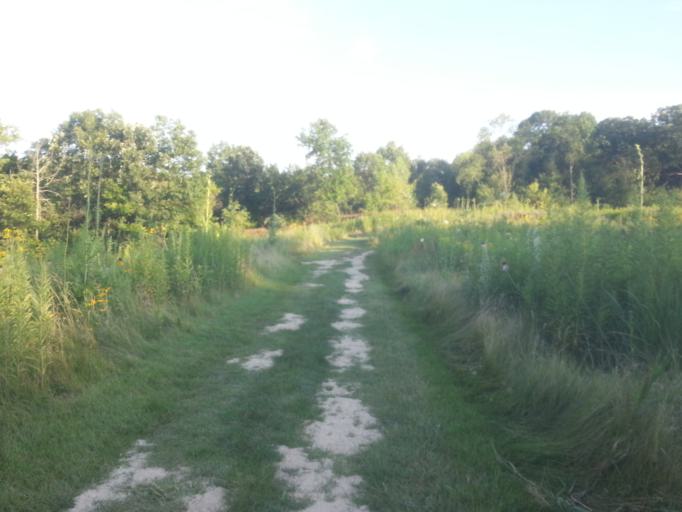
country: US
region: Wisconsin
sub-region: Dane County
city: Middleton
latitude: 43.0694
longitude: -89.4864
